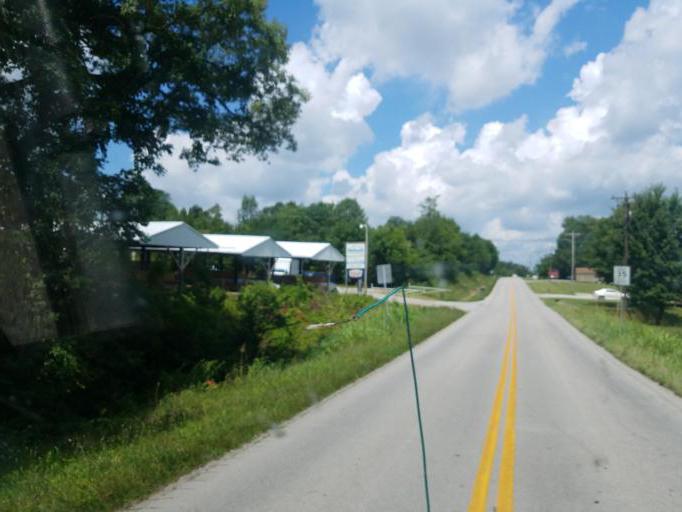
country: US
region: Kentucky
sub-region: Grayson County
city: Leitchfield
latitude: 37.4937
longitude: -86.3008
